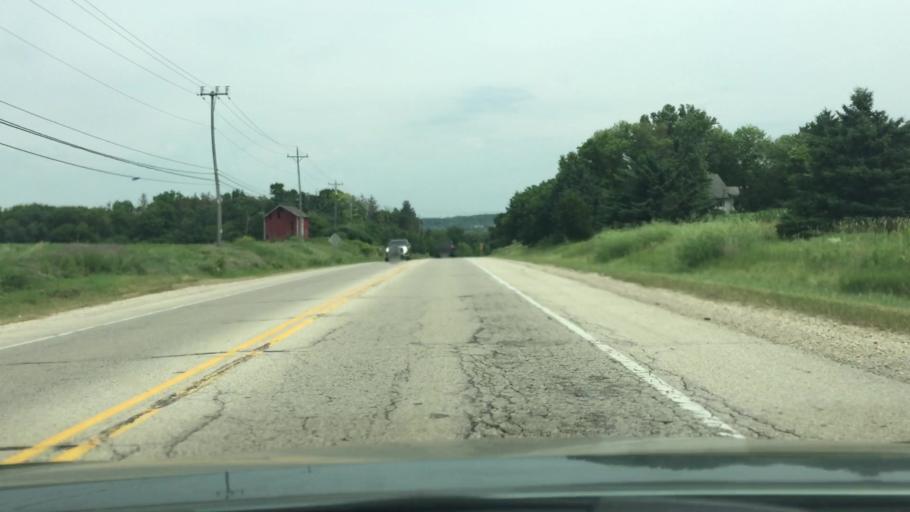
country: US
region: Wisconsin
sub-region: Waukesha County
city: Delafield
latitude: 43.0704
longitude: -88.3657
